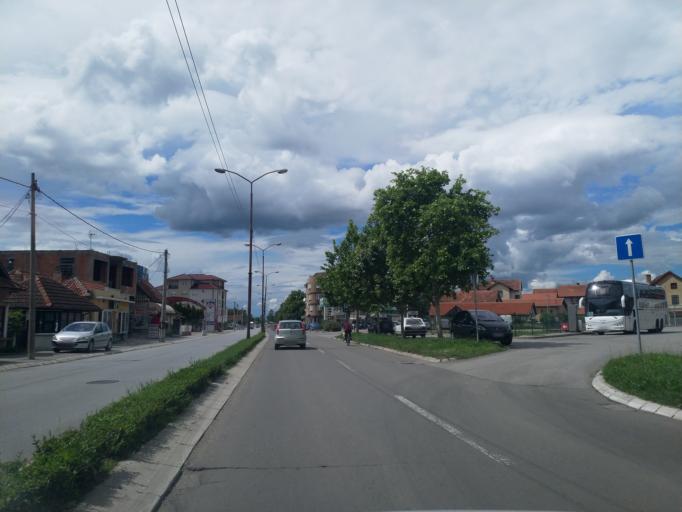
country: RS
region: Central Serbia
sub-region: Pomoravski Okrug
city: Paracin
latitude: 43.8664
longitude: 21.4067
